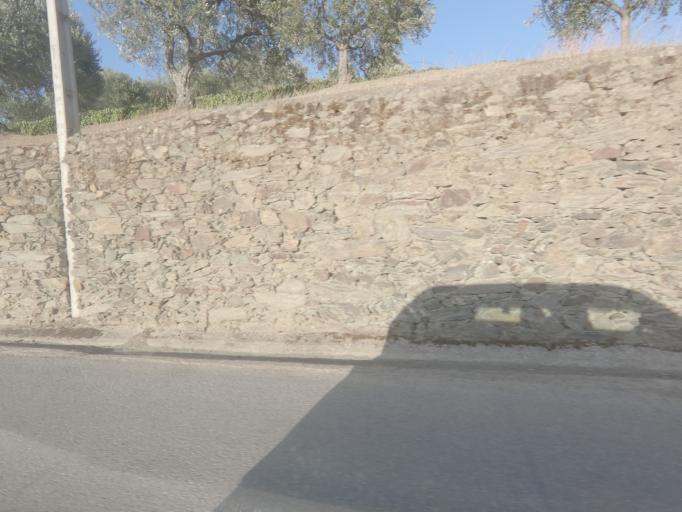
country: PT
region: Viseu
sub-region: Armamar
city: Armamar
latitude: 41.1454
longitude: -7.6792
